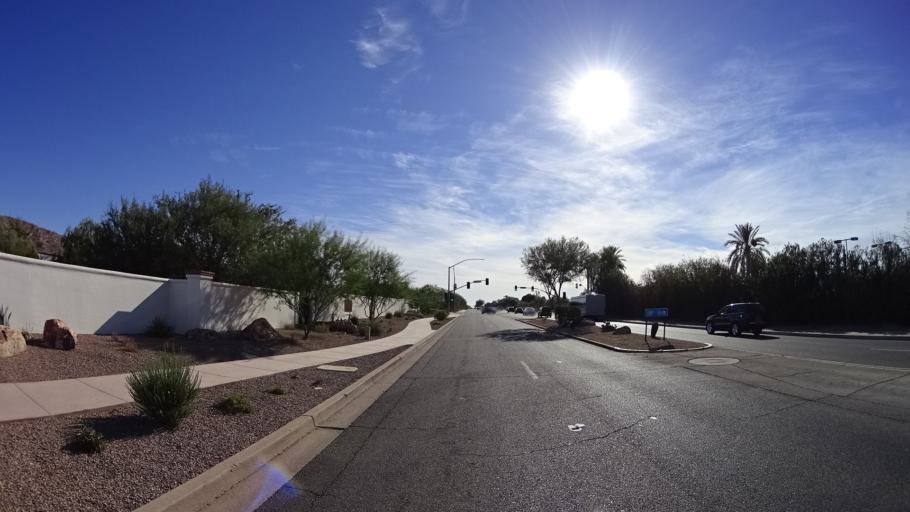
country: US
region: Arizona
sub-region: Maricopa County
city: Paradise Valley
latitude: 33.5311
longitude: -111.9614
